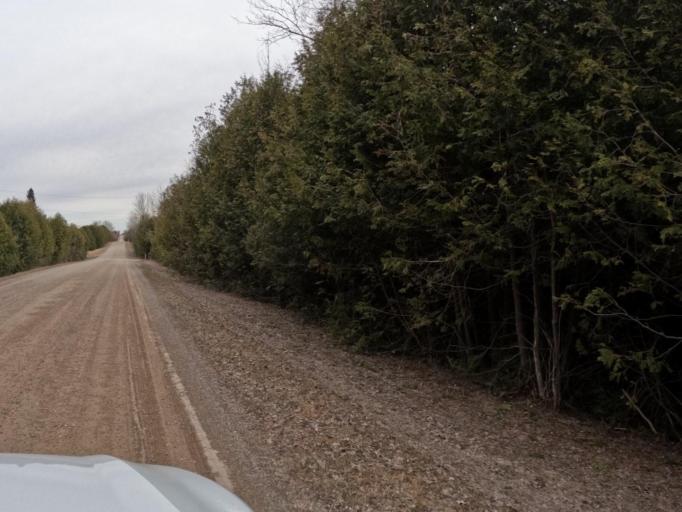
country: CA
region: Ontario
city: Orangeville
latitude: 43.9293
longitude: -80.2575
